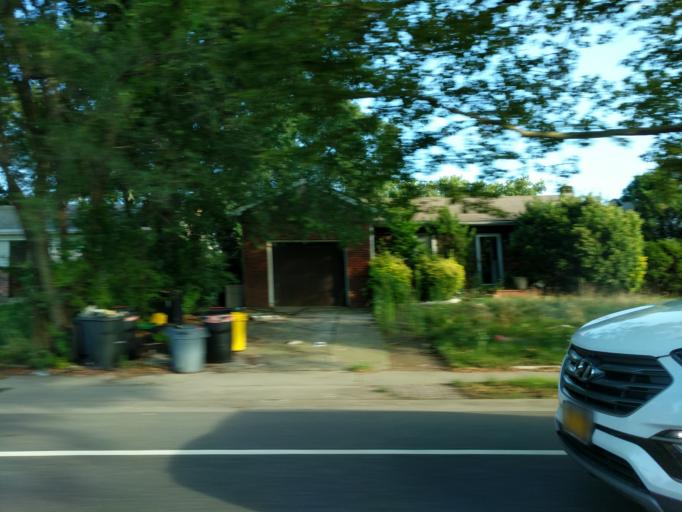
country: US
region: New York
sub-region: Nassau County
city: Hewlett
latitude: 40.6462
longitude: -73.6975
